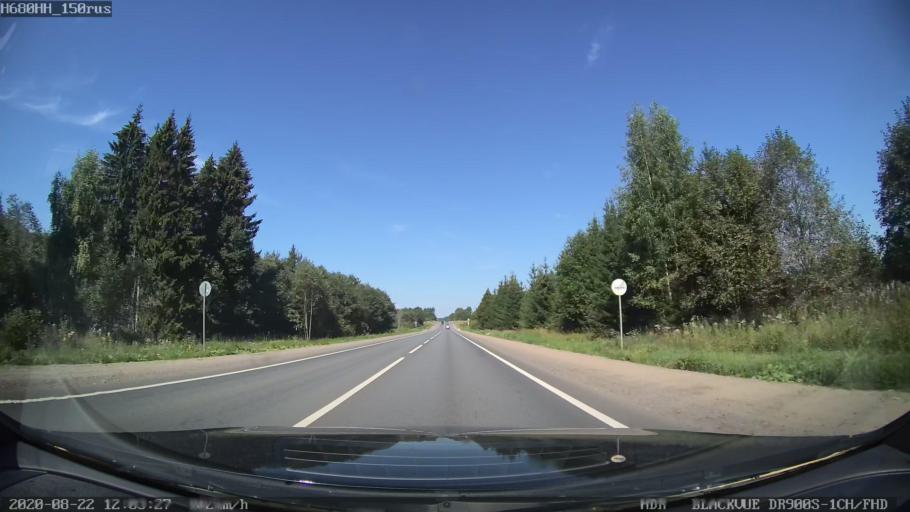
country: RU
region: Tverskaya
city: Rameshki
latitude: 57.2549
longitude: 36.0850
